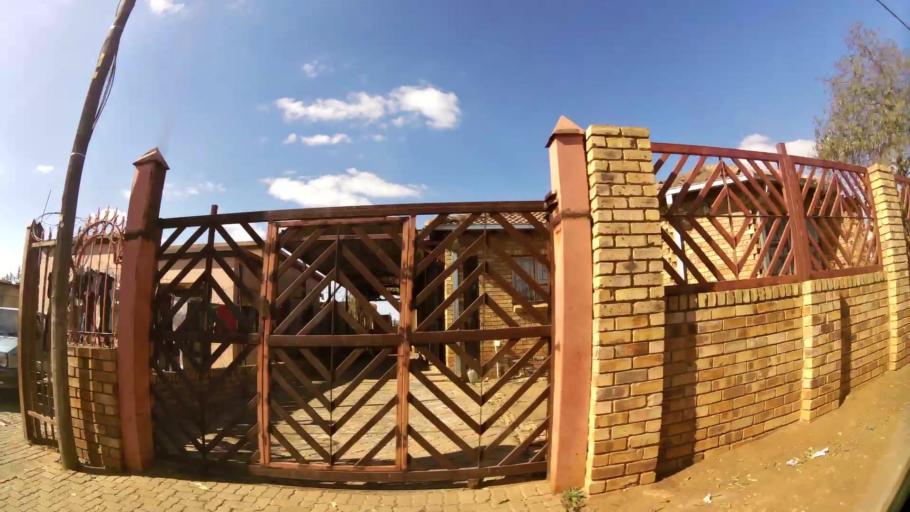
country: ZA
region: Gauteng
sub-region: City of Tshwane Metropolitan Municipality
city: Cullinan
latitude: -25.7219
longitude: 28.4064
